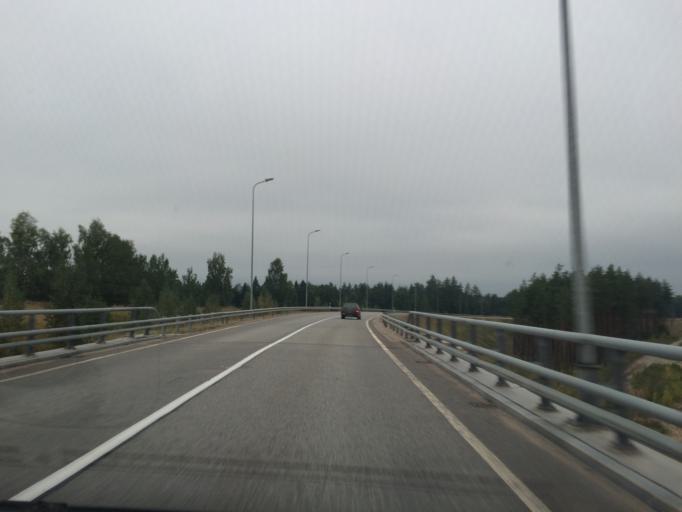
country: LV
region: Varaklani
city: Varaklani
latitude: 56.5298
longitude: 26.5317
